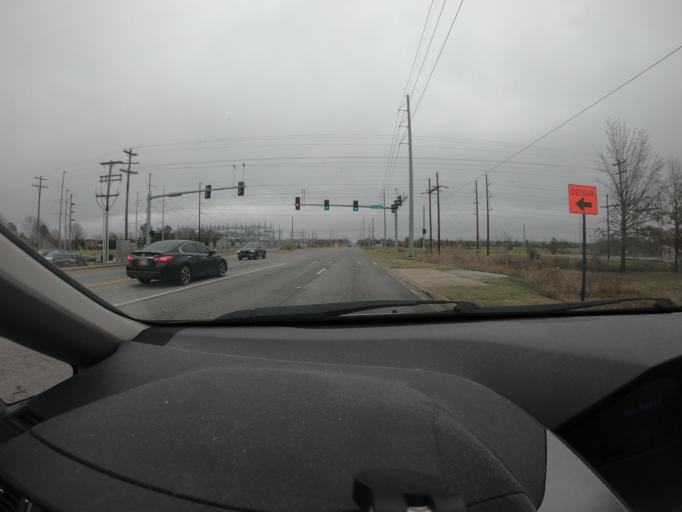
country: US
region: Arkansas
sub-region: Benton County
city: Centerton
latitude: 36.3576
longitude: -94.2496
